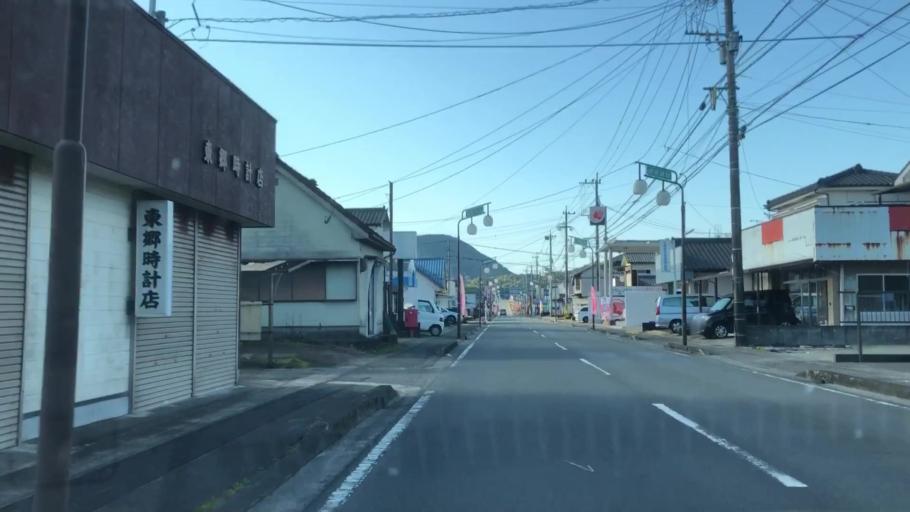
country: JP
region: Kagoshima
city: Satsumasendai
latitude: 31.8634
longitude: 130.3360
